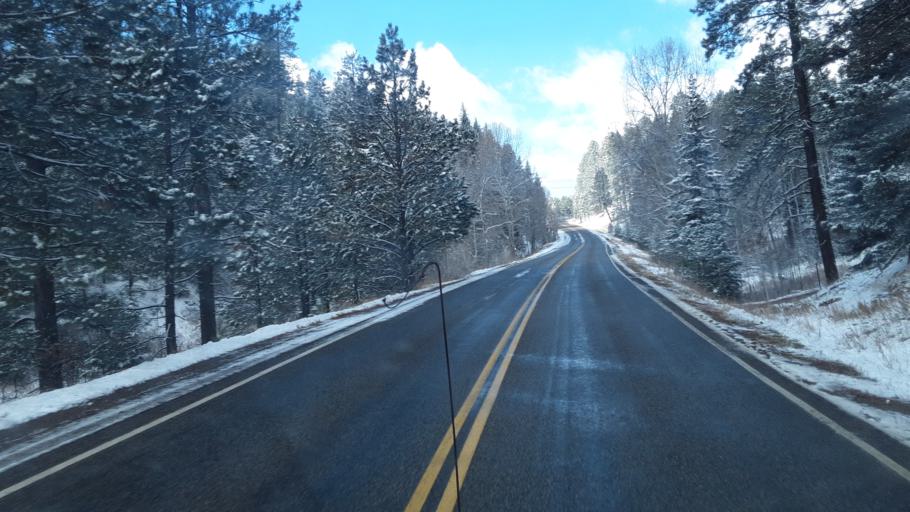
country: US
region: Colorado
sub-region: La Plata County
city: Bayfield
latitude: 37.3525
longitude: -107.6510
